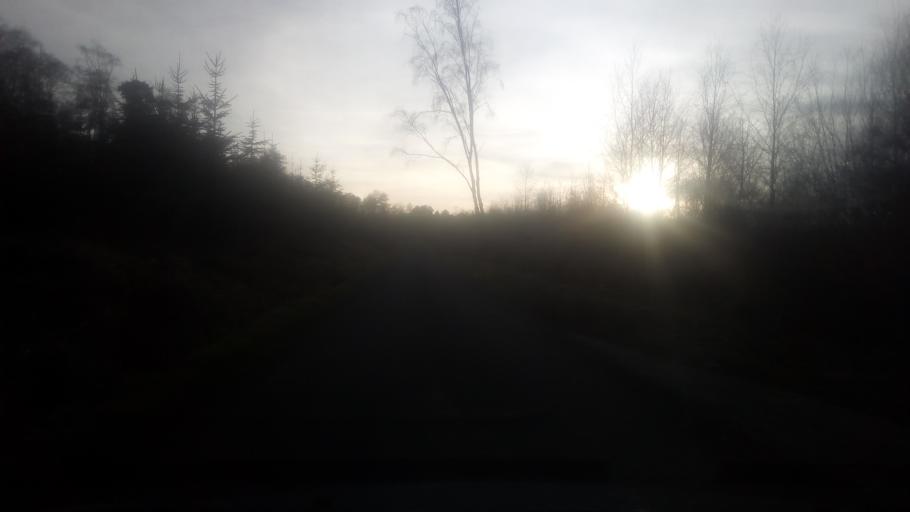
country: GB
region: Scotland
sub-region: The Scottish Borders
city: Jedburgh
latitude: 55.4298
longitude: -2.5536
